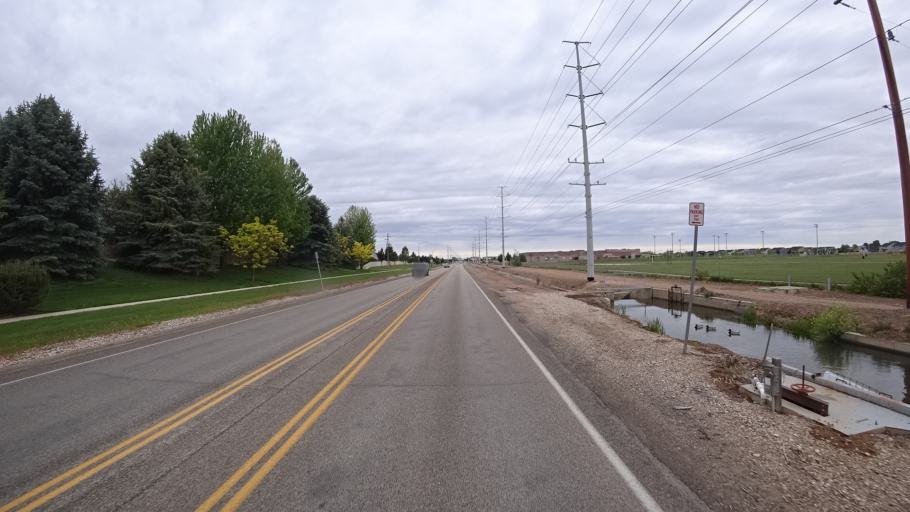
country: US
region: Idaho
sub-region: Ada County
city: Meridian
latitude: 43.6484
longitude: -116.3869
